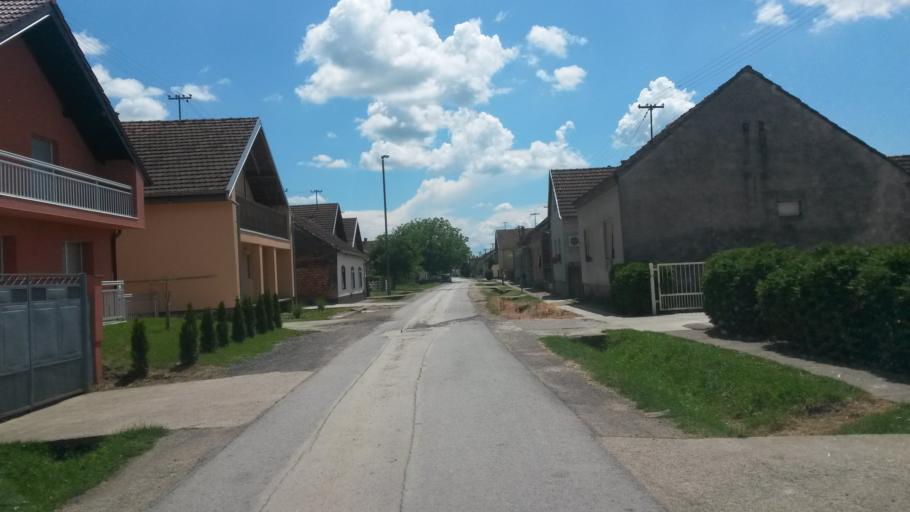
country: HR
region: Vukovarsko-Srijemska
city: Vodinci
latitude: 45.2793
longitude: 18.6106
